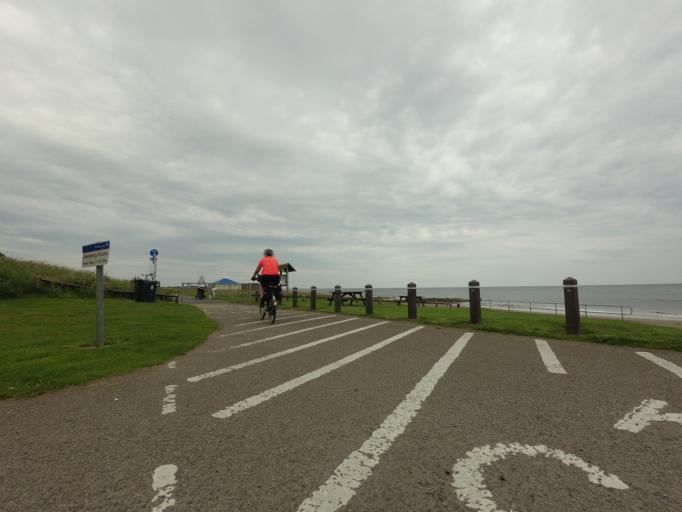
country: GB
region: Scotland
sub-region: Aberdeenshire
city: Banff
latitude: 57.6692
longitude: -2.5429
